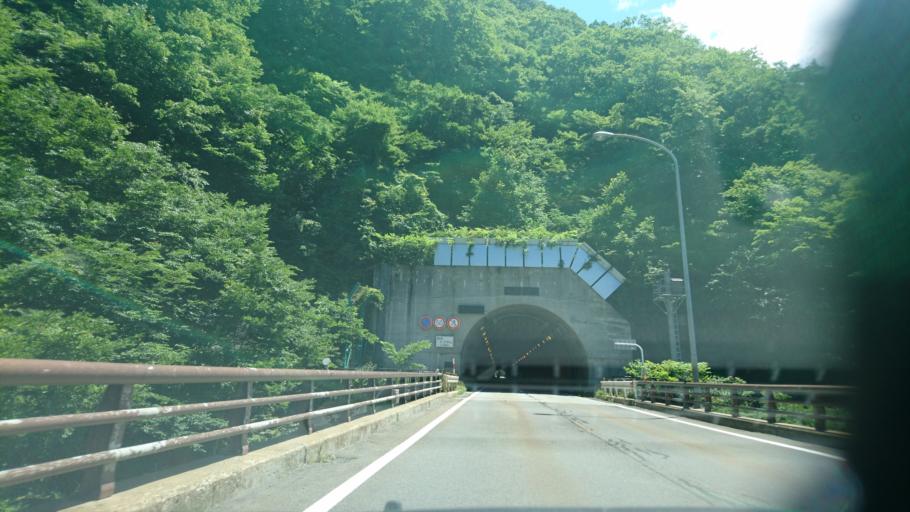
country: JP
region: Iwate
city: Shizukuishi
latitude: 39.7003
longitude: 140.7663
